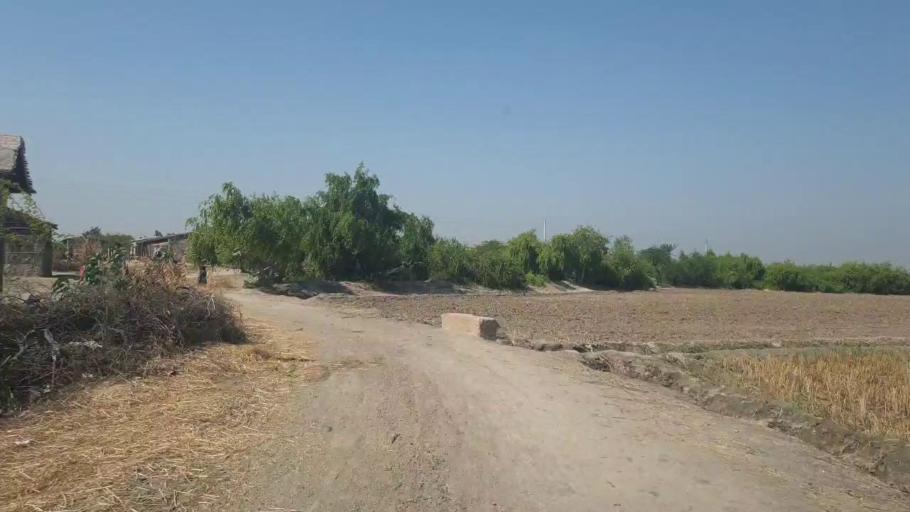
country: PK
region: Sindh
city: Badin
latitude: 24.6945
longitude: 68.8755
